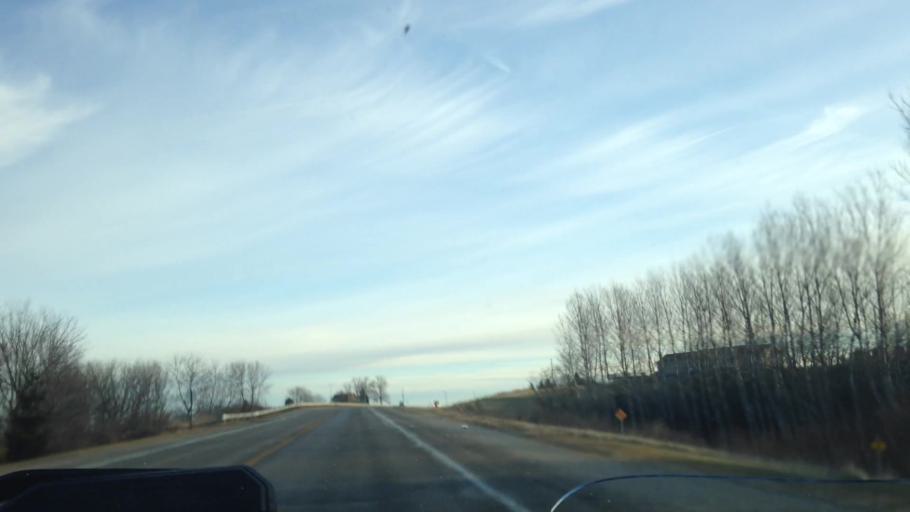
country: US
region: Wisconsin
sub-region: Dodge County
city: Mayville
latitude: 43.5138
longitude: -88.5308
